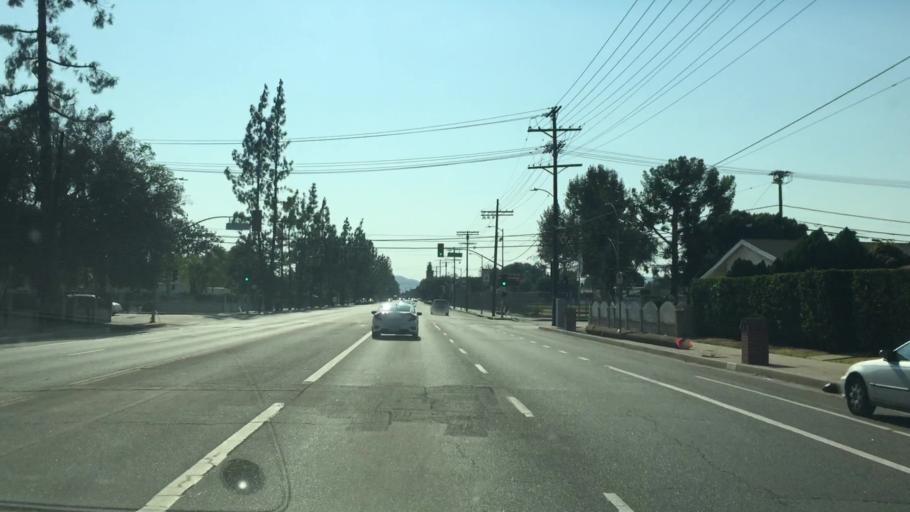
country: US
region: California
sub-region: Los Angeles County
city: Northridge
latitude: 34.2576
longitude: -118.5103
